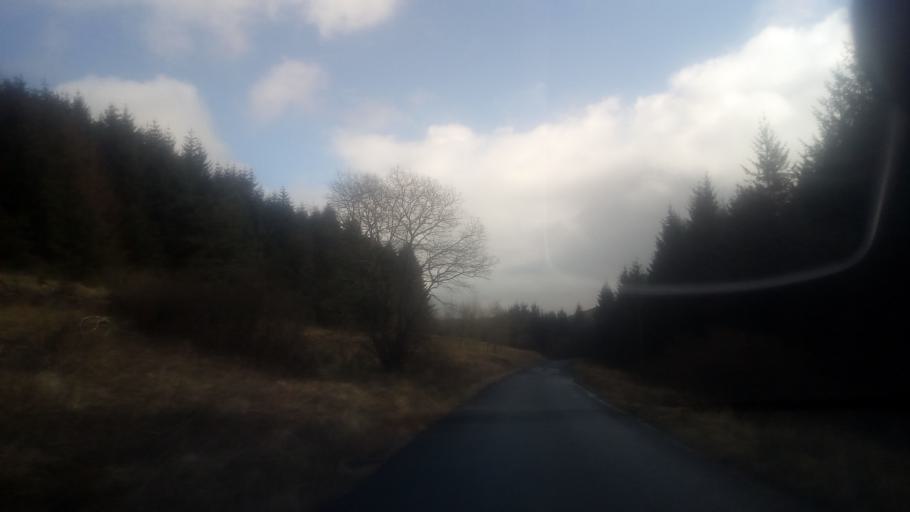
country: GB
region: Scotland
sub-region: The Scottish Borders
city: Innerleithen
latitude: 55.4681
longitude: -3.1387
